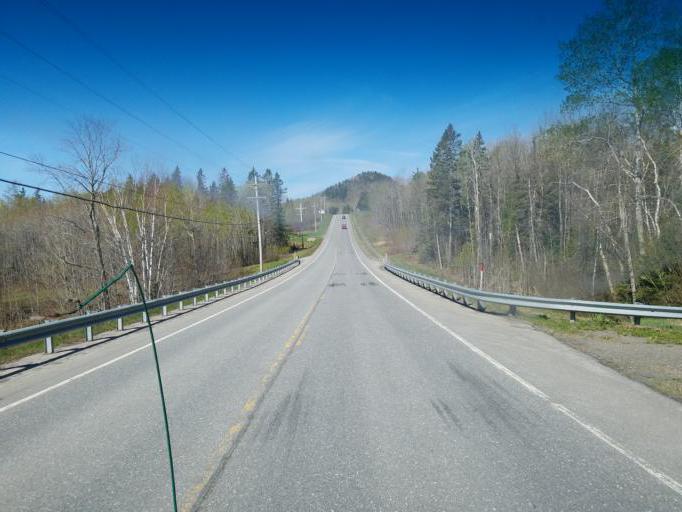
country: US
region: Maine
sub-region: Aroostook County
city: Presque Isle
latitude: 46.6666
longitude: -68.2155
